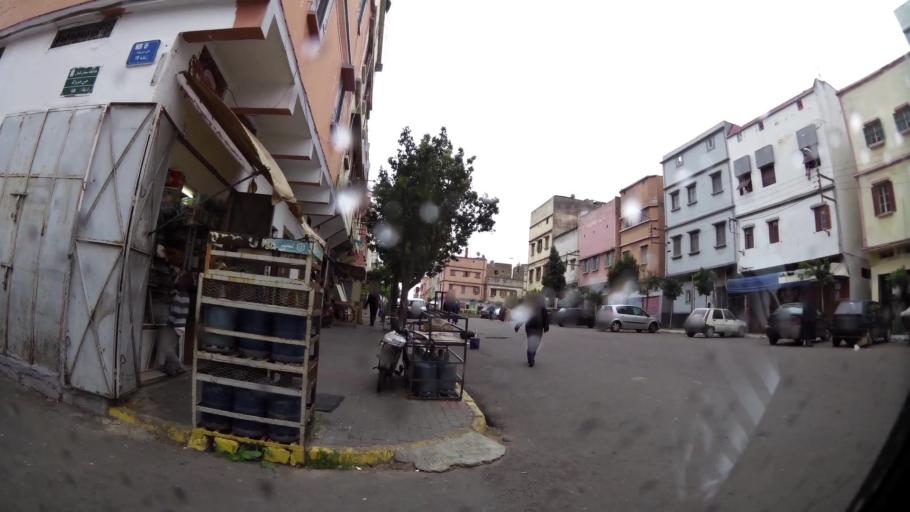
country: MA
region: Grand Casablanca
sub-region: Casablanca
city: Casablanca
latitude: 33.5627
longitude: -7.5651
